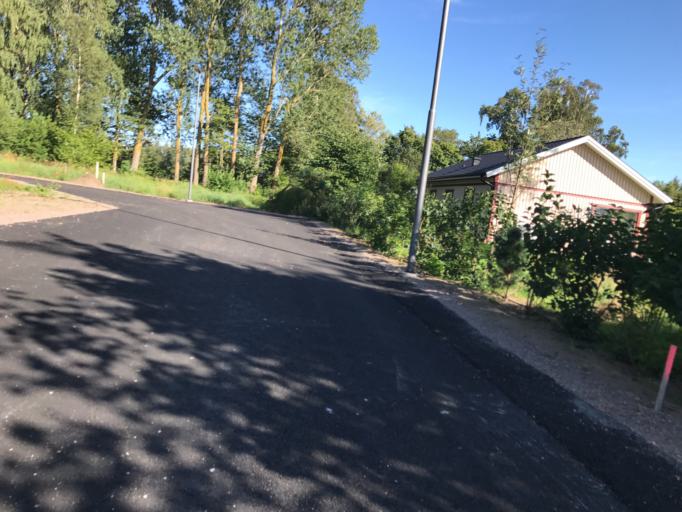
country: SE
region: Skane
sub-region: Bastads Kommun
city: Bastad
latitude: 56.4414
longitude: 12.9080
